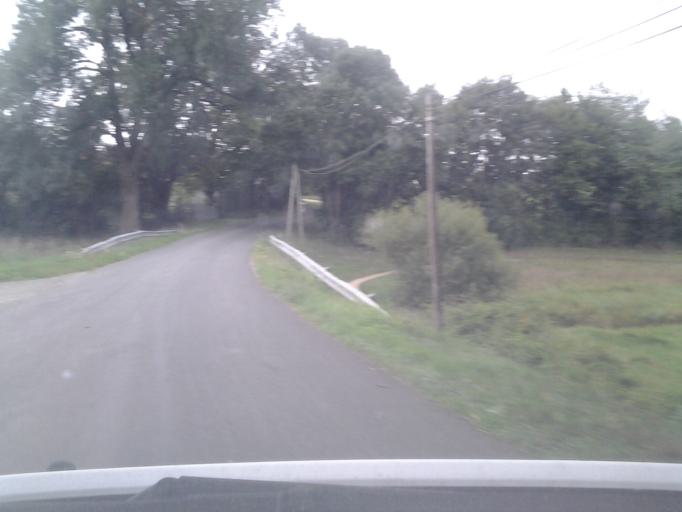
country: FR
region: Pays de la Loire
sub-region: Departement de la Vendee
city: La Roche-sur-Yon
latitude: 46.6982
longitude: -1.4028
